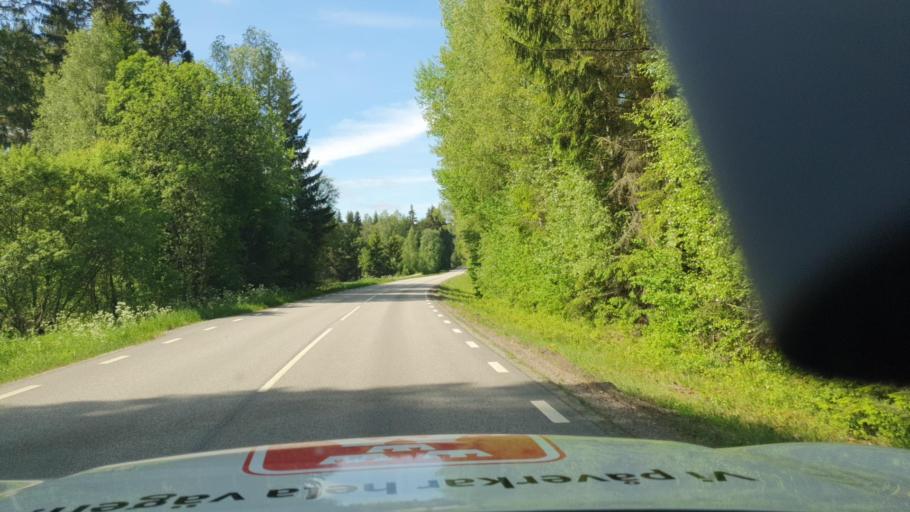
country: SE
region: Vaestra Goetaland
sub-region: Herrljunga Kommun
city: Herrljunga
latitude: 58.0137
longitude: 13.1331
